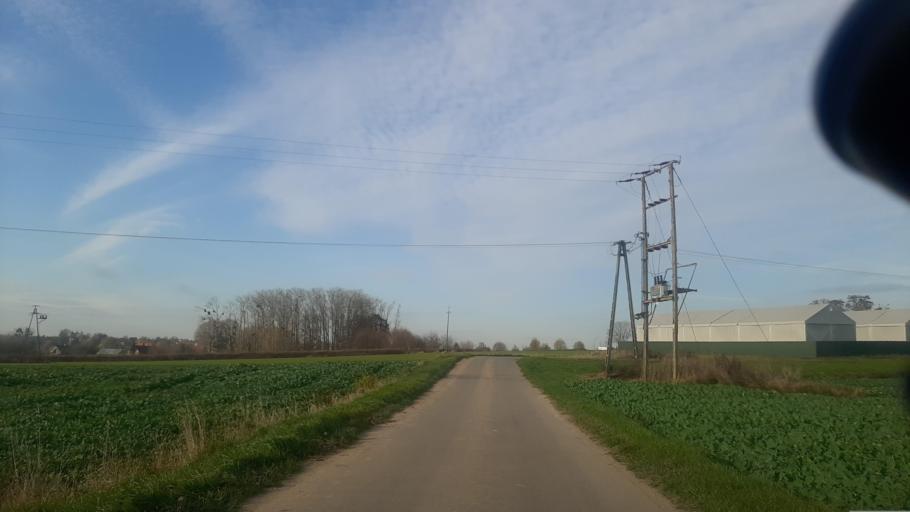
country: PL
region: Lublin Voivodeship
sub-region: Powiat pulawski
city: Markuszow
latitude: 51.3689
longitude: 22.2716
